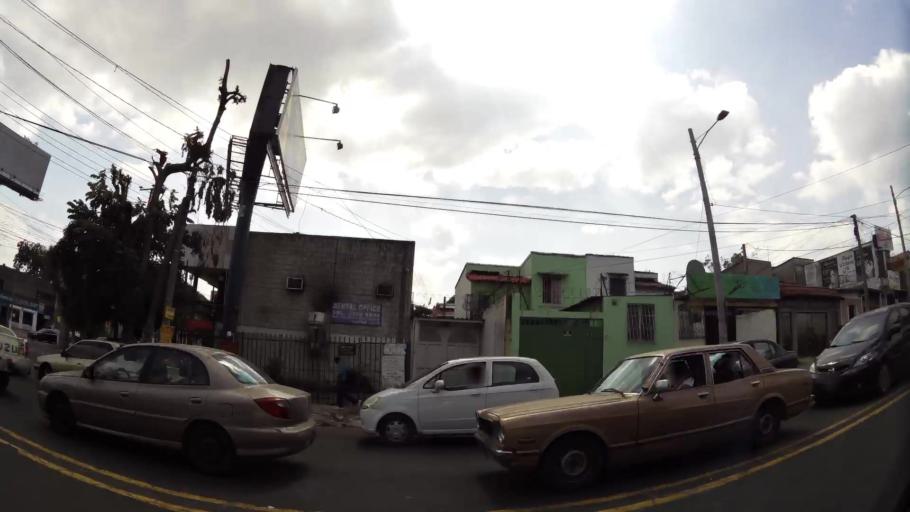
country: SV
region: San Salvador
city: Mejicanos
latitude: 13.7107
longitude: -89.2322
